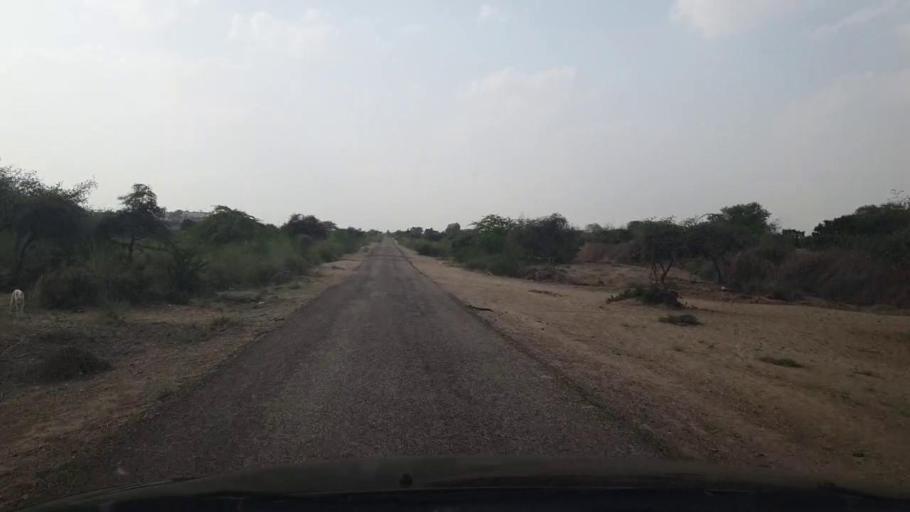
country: PK
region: Sindh
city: Islamkot
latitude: 24.9875
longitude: 70.5748
